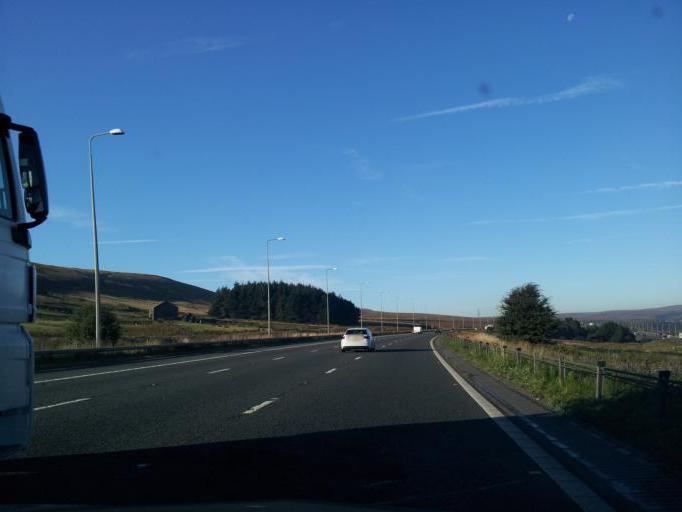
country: GB
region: England
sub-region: Calderdale
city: Ripponden
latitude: 53.6412
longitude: -1.9520
